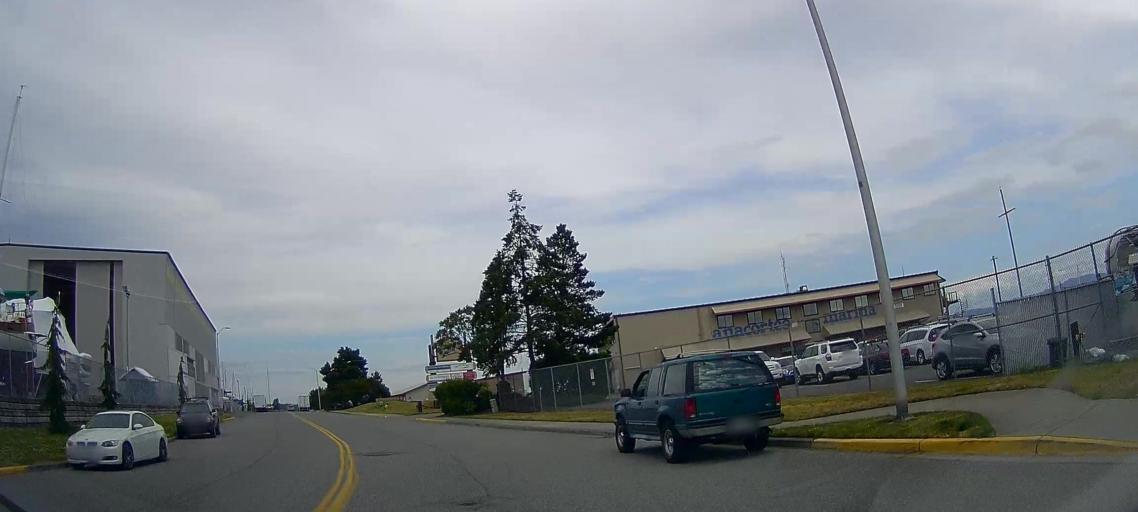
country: US
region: Washington
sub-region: Skagit County
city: Anacortes
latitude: 48.5026
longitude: -122.6068
